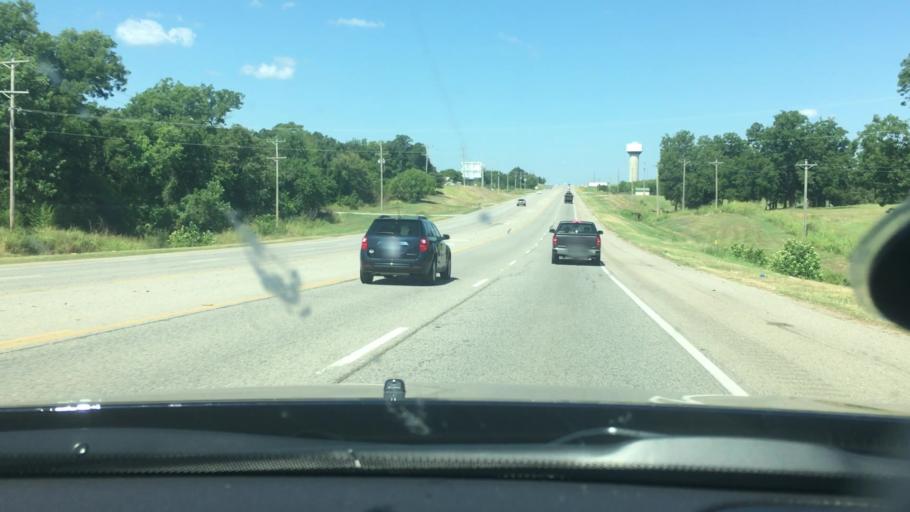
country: US
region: Oklahoma
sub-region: Bryan County
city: Calera
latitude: 33.9979
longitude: -96.4424
